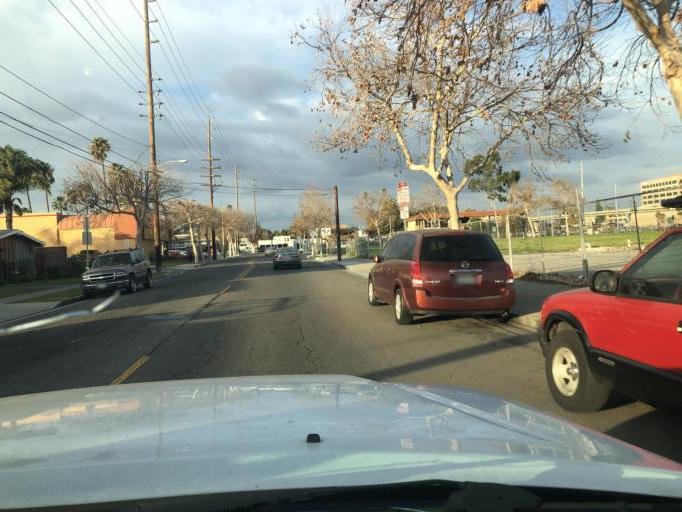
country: US
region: California
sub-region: Orange County
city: Tustin
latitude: 33.7441
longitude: -117.8449
